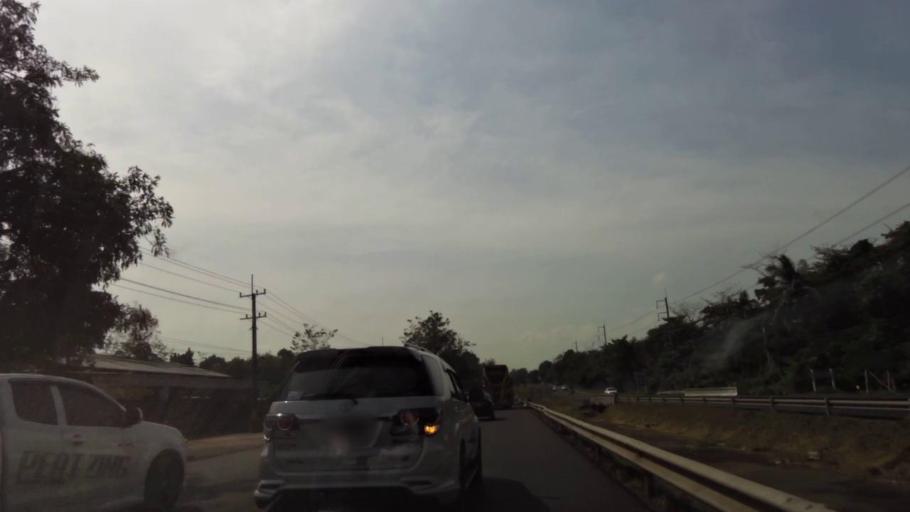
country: TH
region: Chanthaburi
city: Chanthaburi
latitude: 12.6646
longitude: 102.0852
